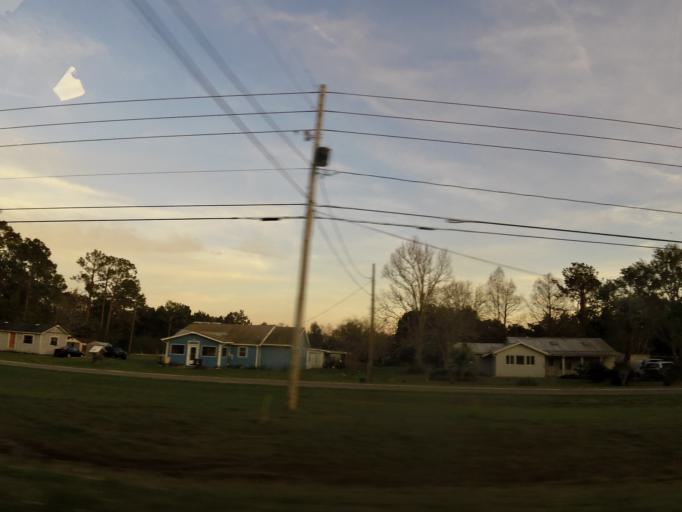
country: US
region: Florida
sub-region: Volusia County
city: North DeLand
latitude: 29.0864
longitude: -81.3036
